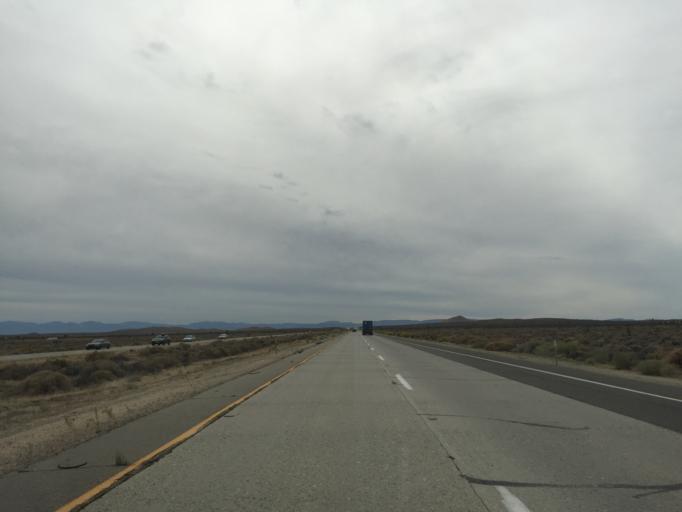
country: US
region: California
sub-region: Kern County
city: Rosamond
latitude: 34.9469
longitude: -118.1617
